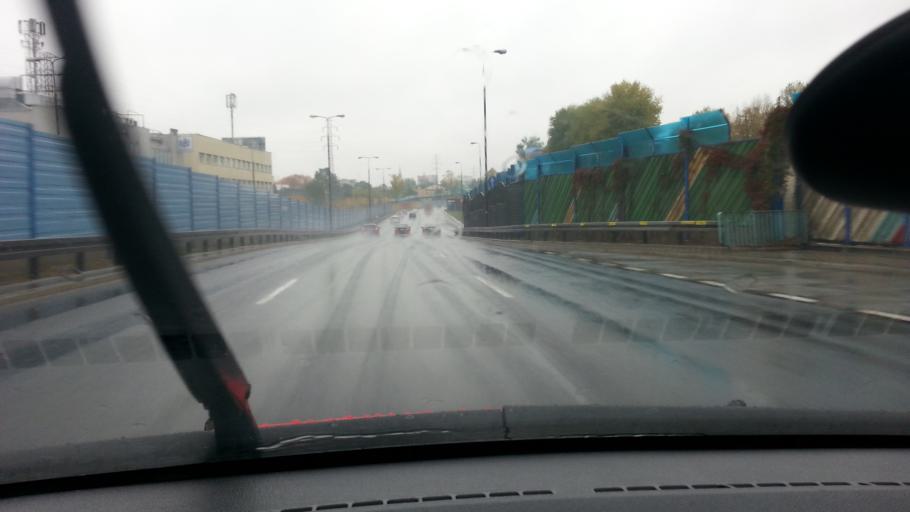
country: PL
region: Masovian Voivodeship
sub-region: Warszawa
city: Wola
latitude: 52.2467
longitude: 20.9575
